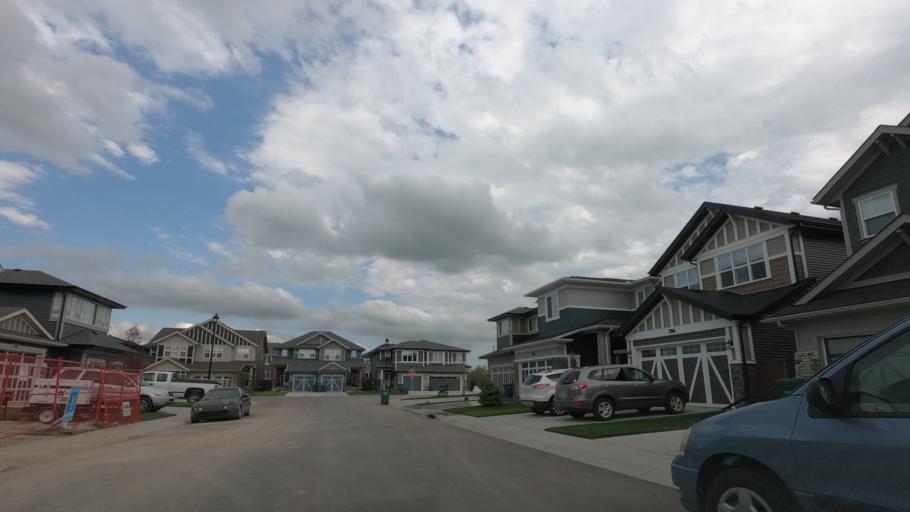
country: CA
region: Alberta
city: Airdrie
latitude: 51.2568
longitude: -113.9886
